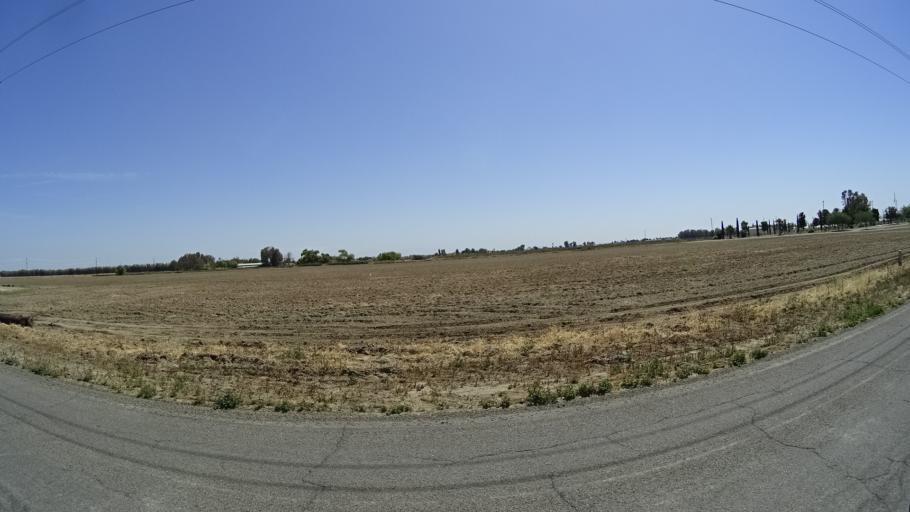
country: US
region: California
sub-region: Kings County
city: Lemoore
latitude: 36.2518
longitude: -119.7988
